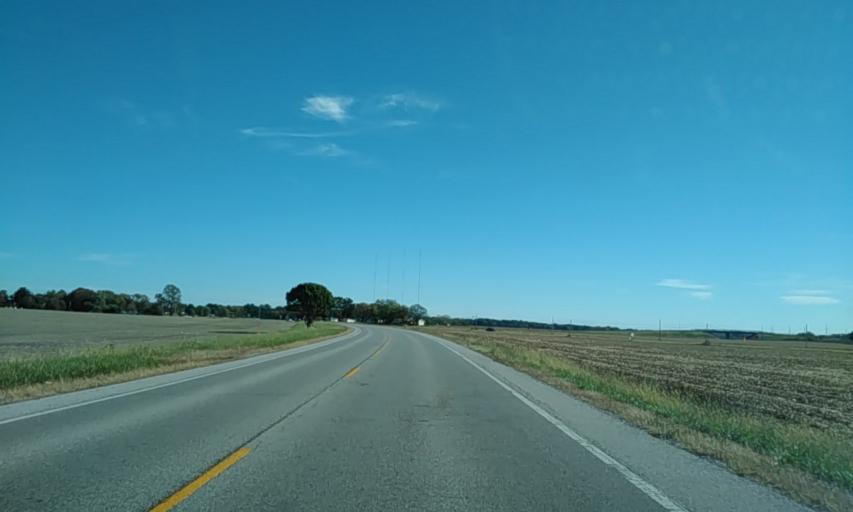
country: US
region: Illinois
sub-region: Madison County
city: Highland
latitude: 38.7511
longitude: -89.6678
